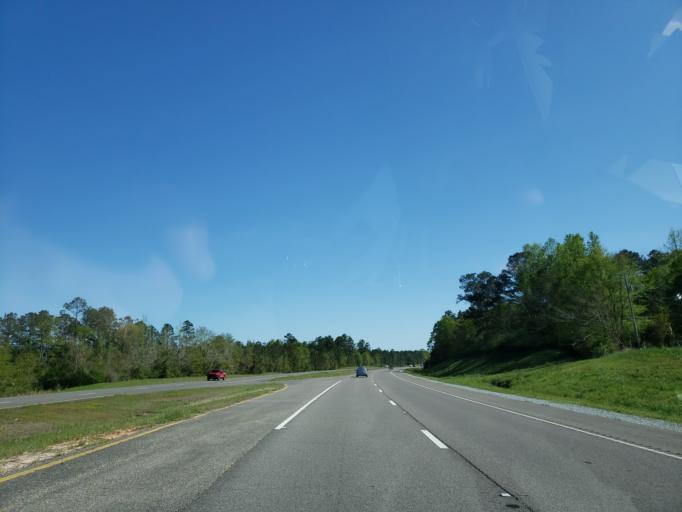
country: US
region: Mississippi
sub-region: Harrison County
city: Saucier
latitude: 30.6323
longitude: -89.1115
